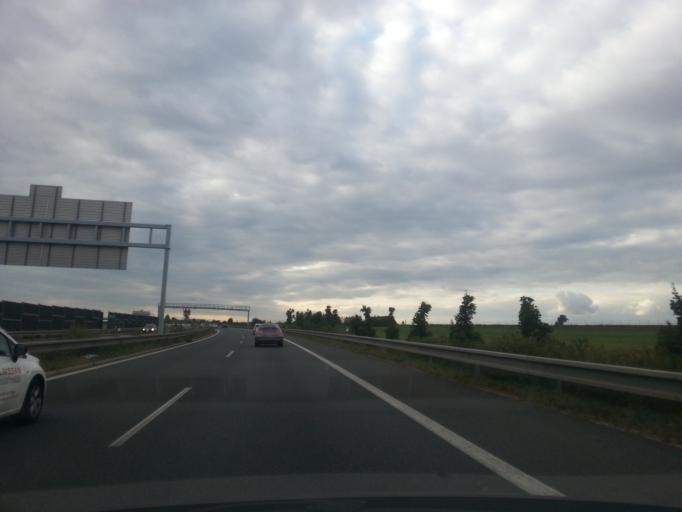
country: CZ
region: Central Bohemia
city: Hostivice
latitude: 50.0829
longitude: 14.2814
